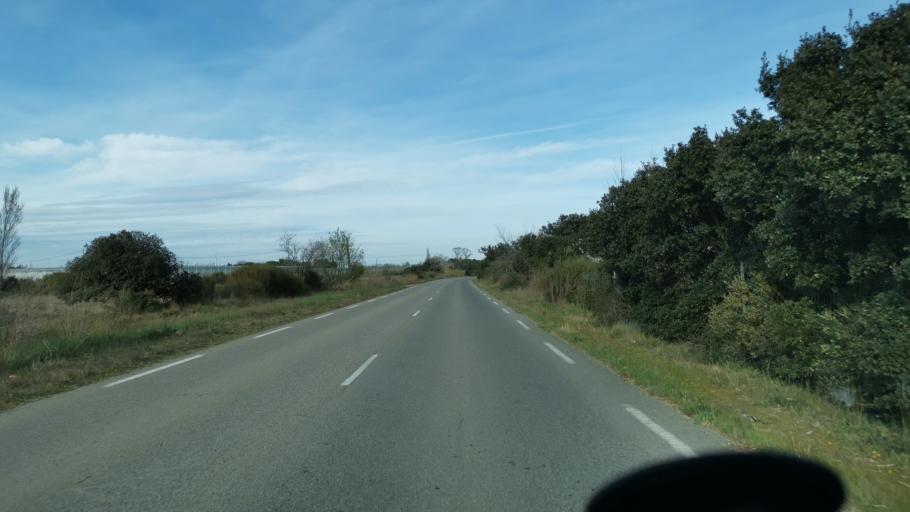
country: FR
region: Provence-Alpes-Cote d'Azur
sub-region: Departement des Bouches-du-Rhone
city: Saint-Martin-de-Crau
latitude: 43.5735
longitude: 4.7486
